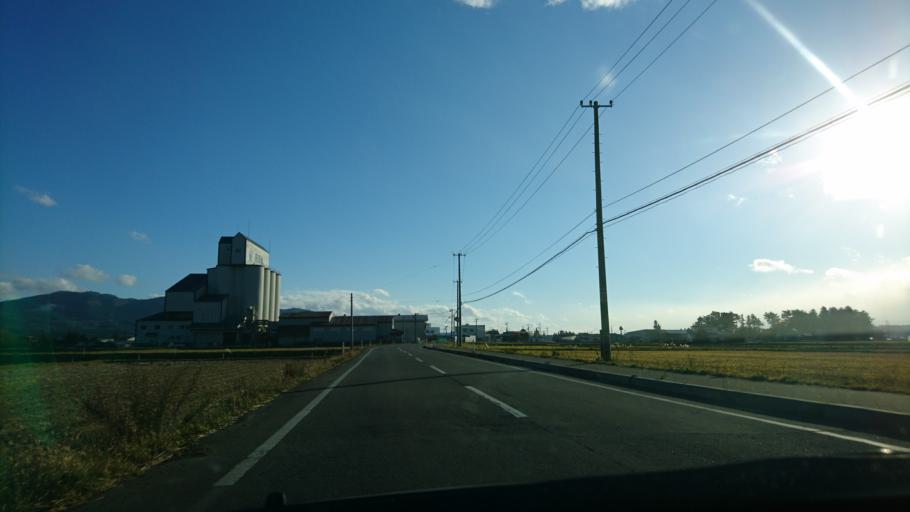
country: JP
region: Iwate
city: Mizusawa
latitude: 39.0700
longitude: 141.1469
